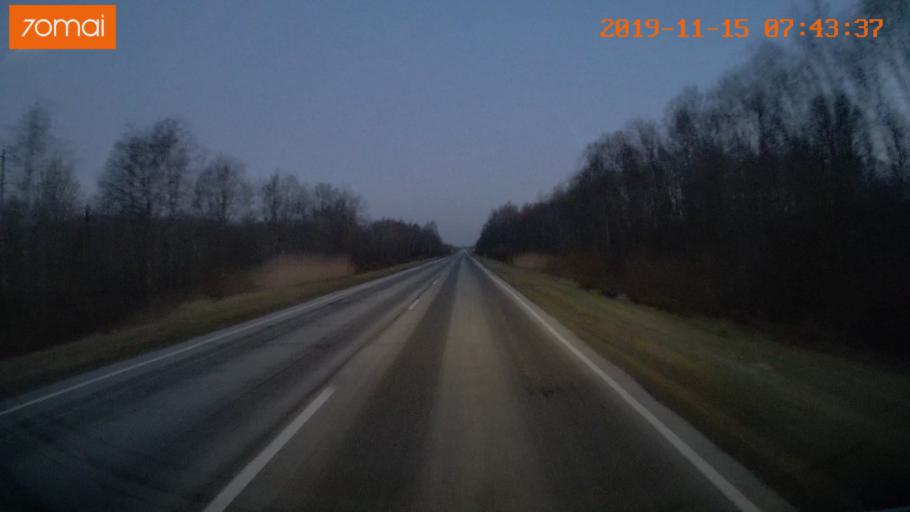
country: RU
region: Vologda
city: Sheksna
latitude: 58.8019
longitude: 38.3296
